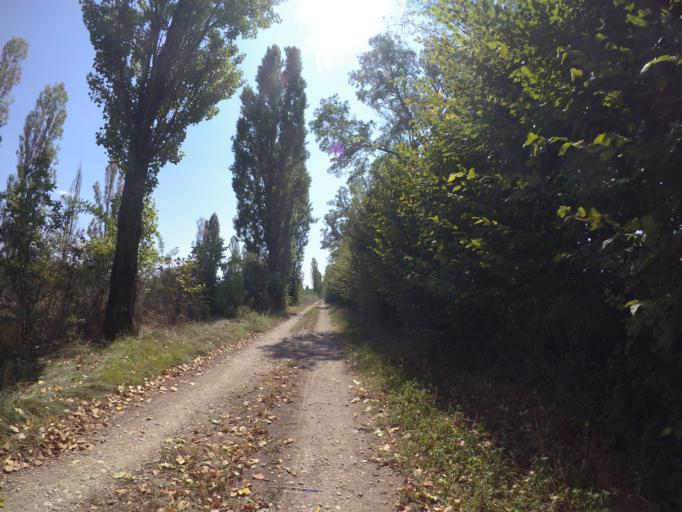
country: IT
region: Friuli Venezia Giulia
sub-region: Provincia di Udine
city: Codroipo
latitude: 45.9600
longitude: 13.0108
